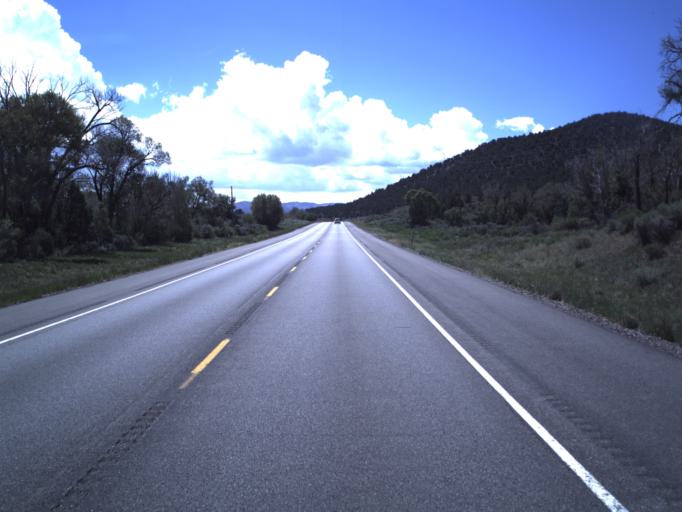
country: US
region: Utah
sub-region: Garfield County
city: Panguitch
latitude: 37.7999
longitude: -112.3995
